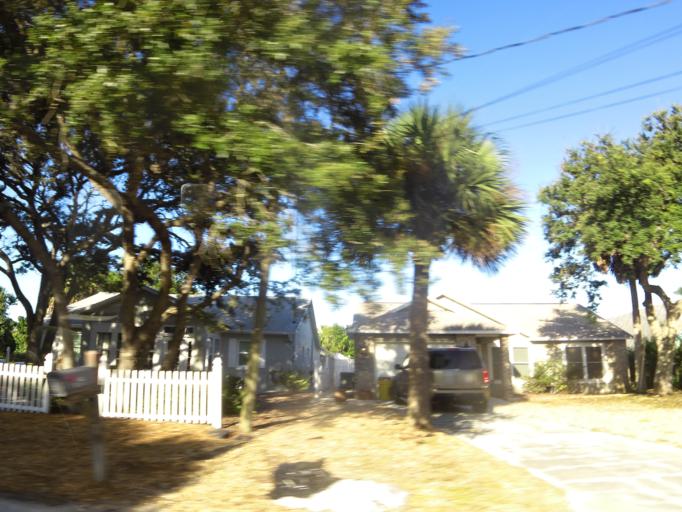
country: US
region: Florida
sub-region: Flagler County
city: Flagler Beach
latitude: 29.4561
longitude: -81.1191
